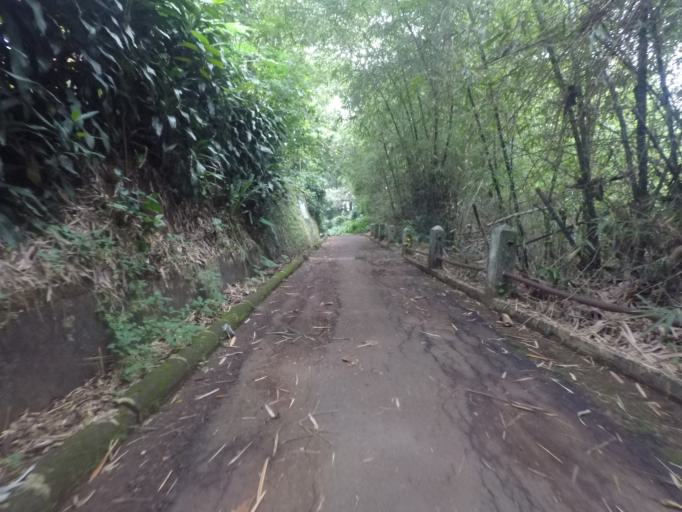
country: ID
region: West Java
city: Ciampea
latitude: -6.5501
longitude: 106.7498
